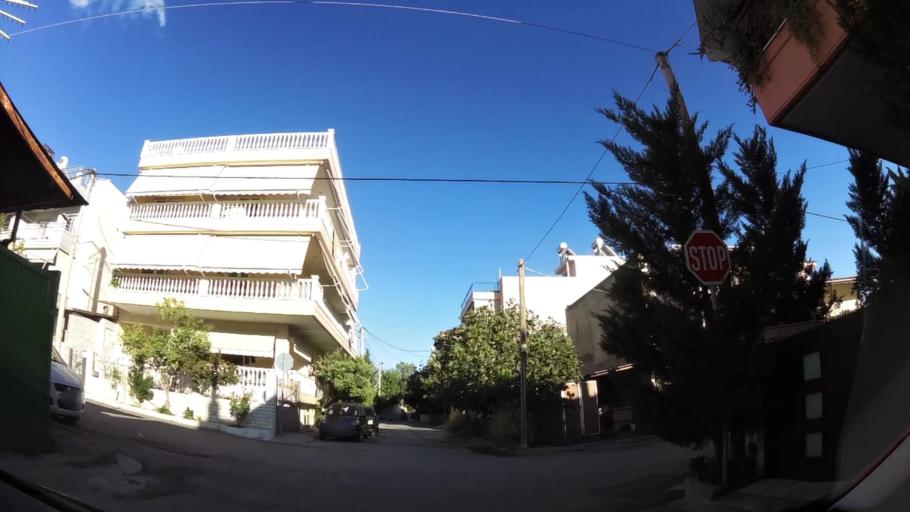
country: GR
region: Attica
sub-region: Nomarchia Anatolikis Attikis
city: Acharnes
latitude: 38.0930
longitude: 23.7243
